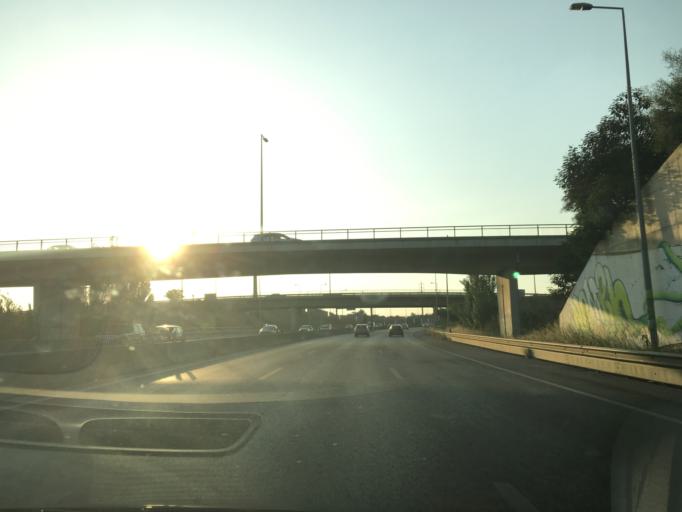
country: PT
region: Lisbon
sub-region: Sintra
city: Rio de Mouro
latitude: 38.7672
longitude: -9.3141
